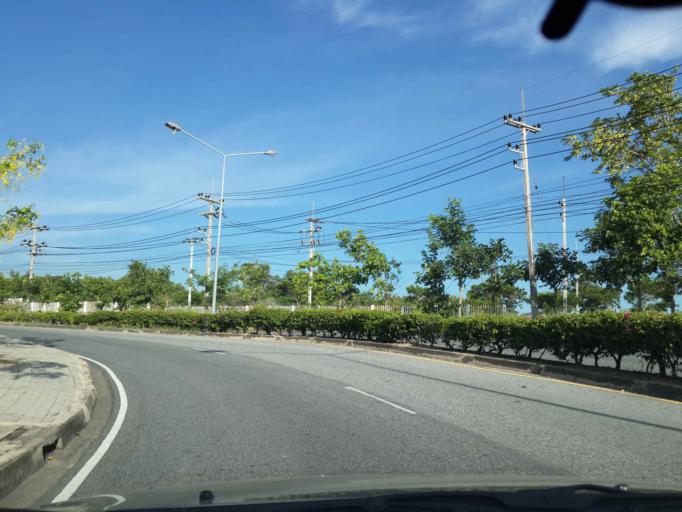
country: TH
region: Chon Buri
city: Phatthaya
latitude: 12.9168
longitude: 100.9979
